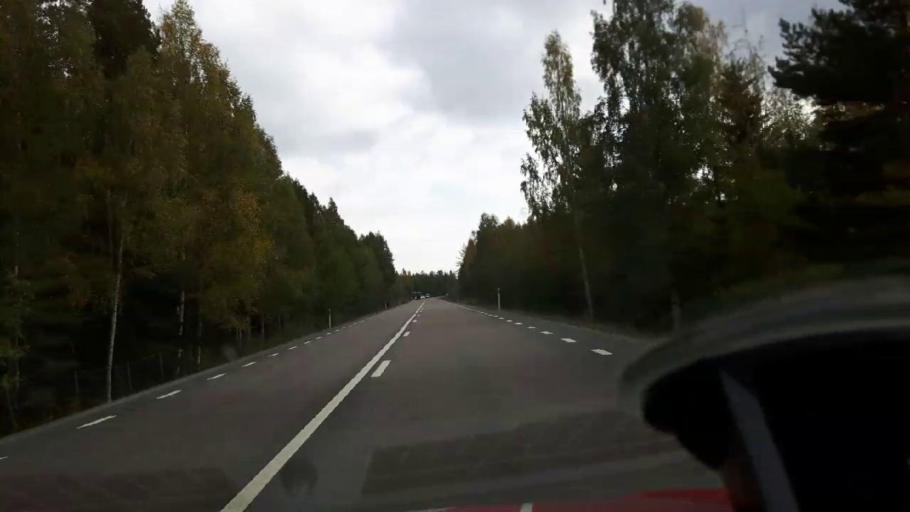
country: SE
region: Gaevleborg
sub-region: Bollnas Kommun
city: Kilafors
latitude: 61.2728
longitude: 16.5313
